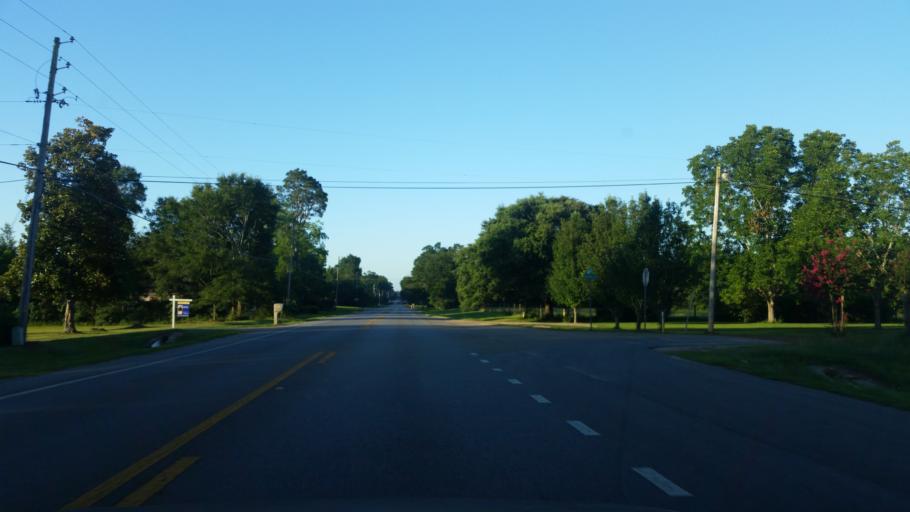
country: US
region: Florida
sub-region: Escambia County
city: Cantonment
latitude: 30.5878
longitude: -87.3493
